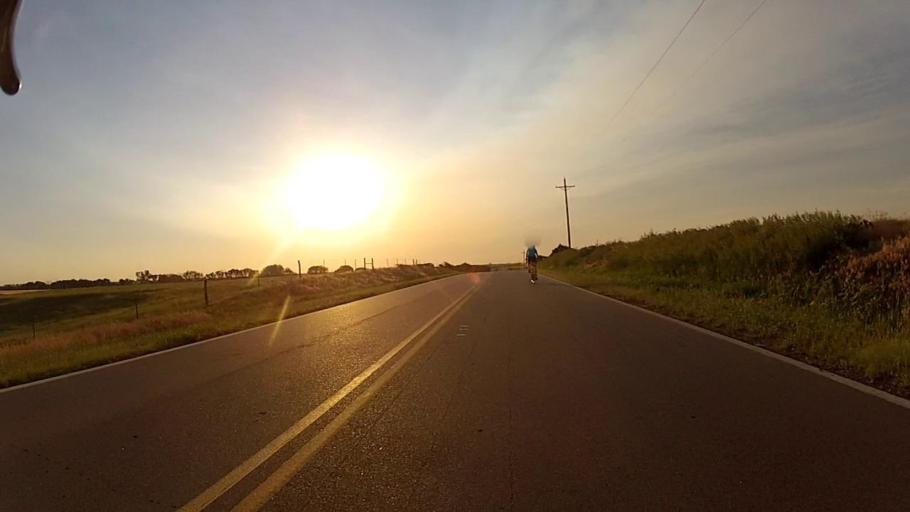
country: US
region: Kansas
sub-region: Harper County
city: Anthony
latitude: 37.1527
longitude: -97.9408
